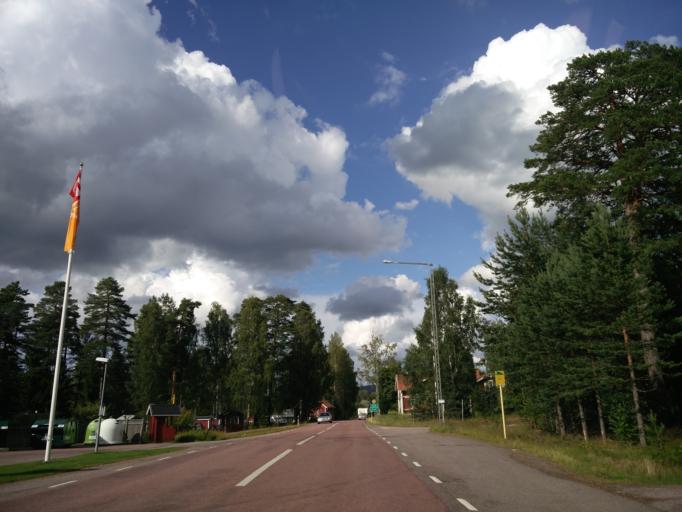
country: SE
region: Vaermland
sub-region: Torsby Kommun
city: Torsby
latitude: 60.2748
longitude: 13.0294
